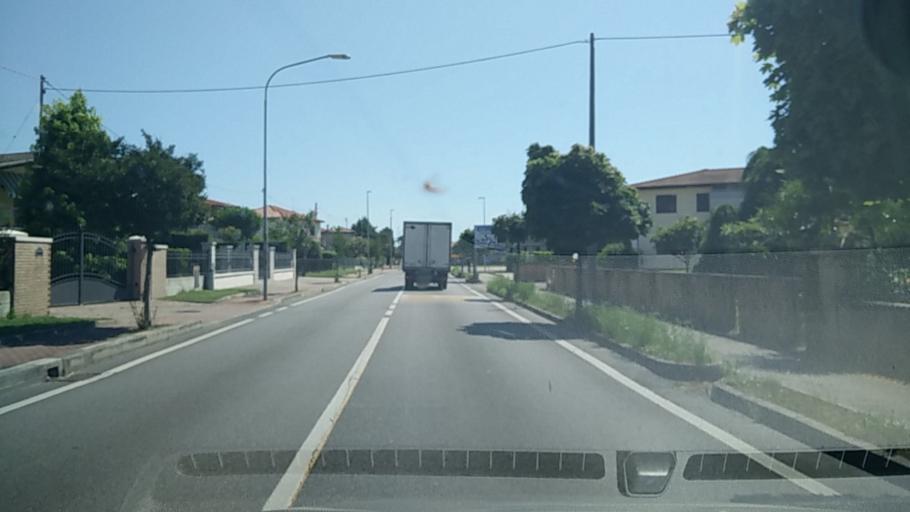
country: IT
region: Veneto
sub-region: Provincia di Venezia
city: Camponogara
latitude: 45.3840
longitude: 12.0885
